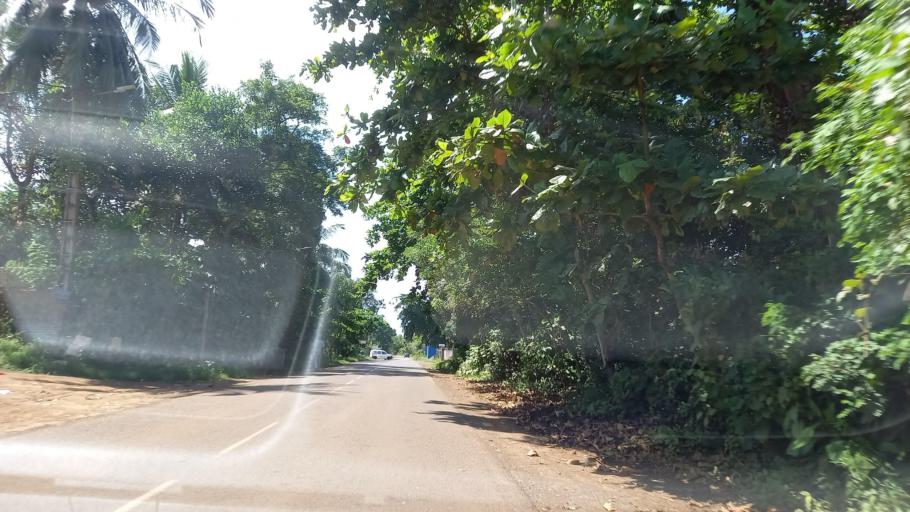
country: YT
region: Bandraboua
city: Bandraboua
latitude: -12.7226
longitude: 45.1244
